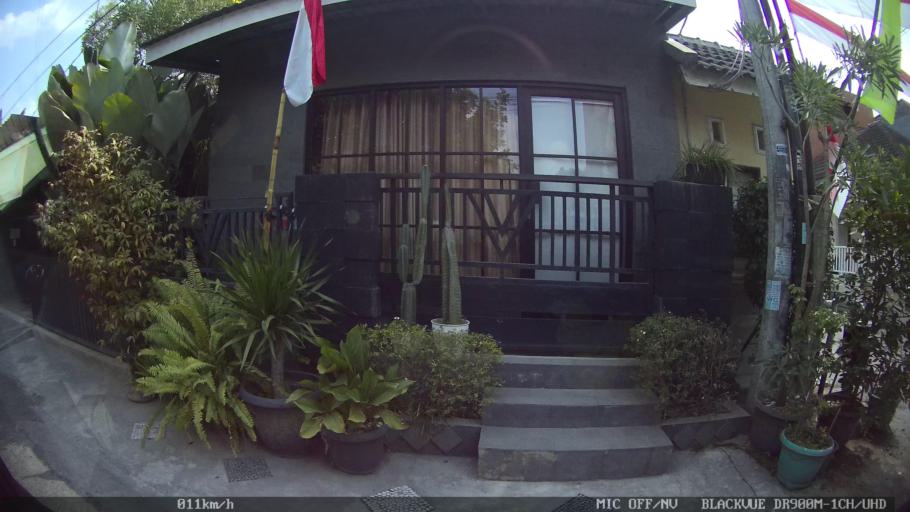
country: ID
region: Daerah Istimewa Yogyakarta
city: Depok
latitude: -7.8020
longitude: 110.4075
